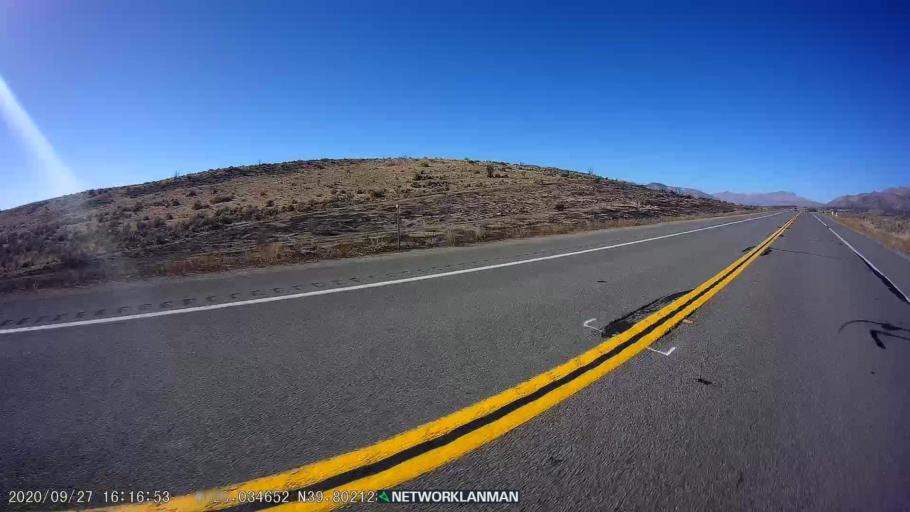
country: US
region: Nevada
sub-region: Washoe County
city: Cold Springs
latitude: 39.8033
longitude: -120.0348
